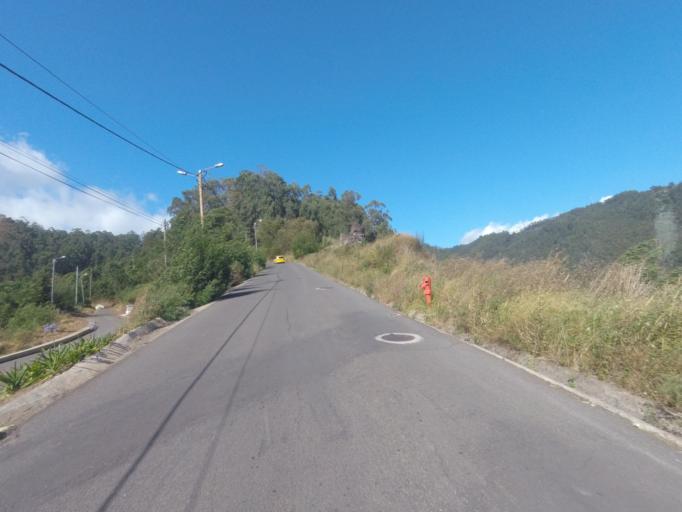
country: PT
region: Madeira
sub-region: Ribeira Brava
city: Campanario
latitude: 32.6822
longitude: -17.0239
